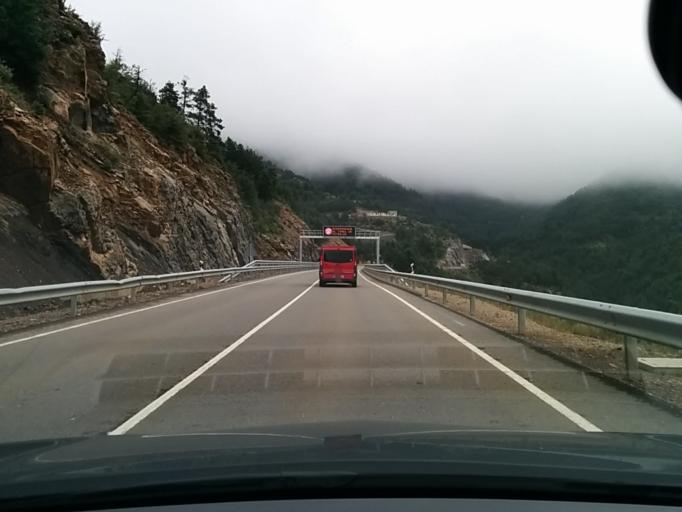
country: ES
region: Aragon
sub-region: Provincia de Huesca
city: Fiscal
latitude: 42.4663
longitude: -0.1962
